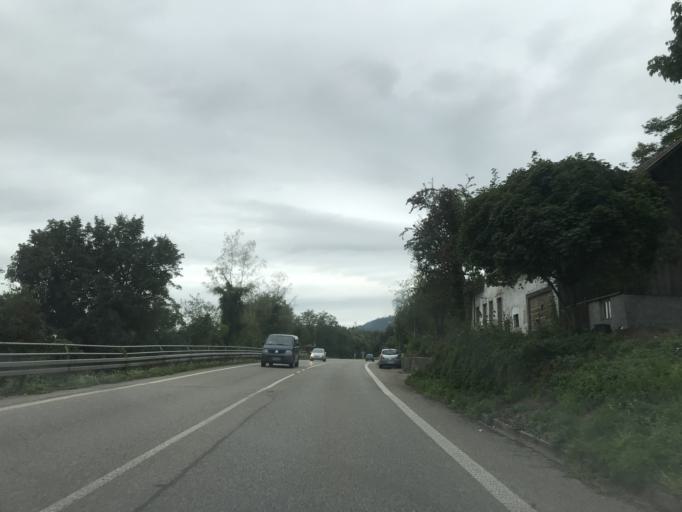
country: DE
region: Baden-Wuerttemberg
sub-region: Freiburg Region
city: Murg
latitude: 47.5571
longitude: 8.0034
